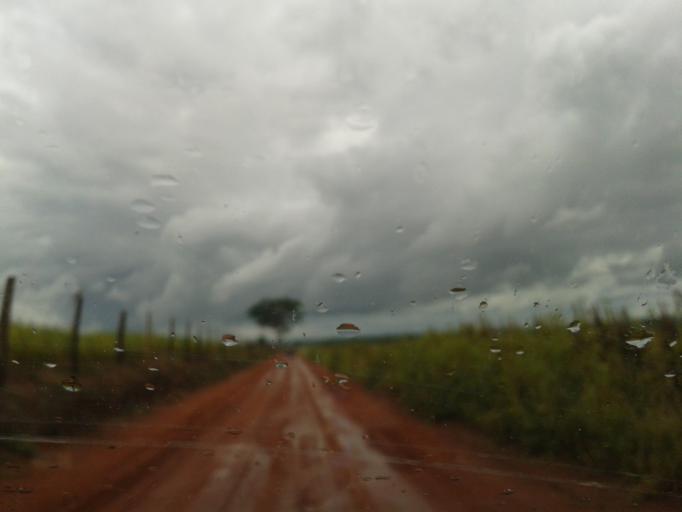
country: BR
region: Minas Gerais
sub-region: Santa Vitoria
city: Santa Vitoria
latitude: -18.6966
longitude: -49.9599
